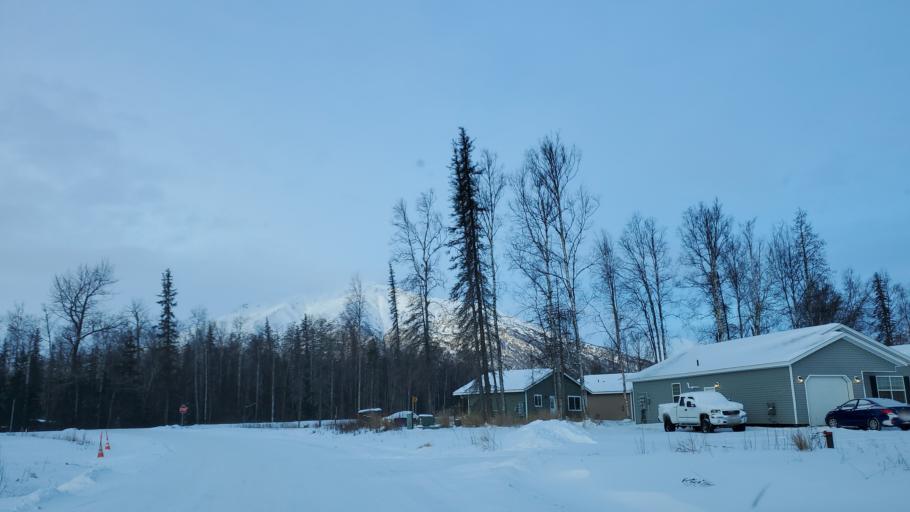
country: US
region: Alaska
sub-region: Matanuska-Susitna Borough
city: Fishhook
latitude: 61.6841
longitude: -149.2455
